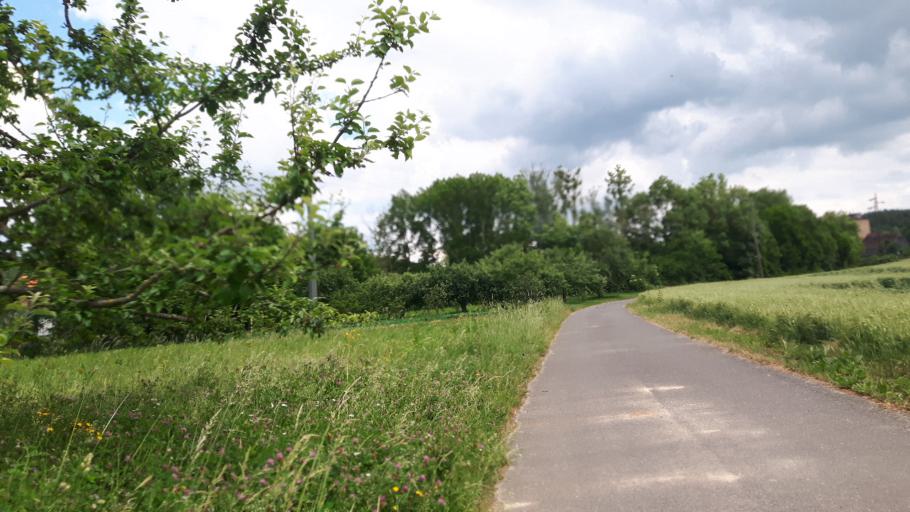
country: DE
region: Baden-Wuerttemberg
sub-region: Regierungsbezirk Stuttgart
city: Grunsfeld
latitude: 49.5975
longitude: 9.7800
